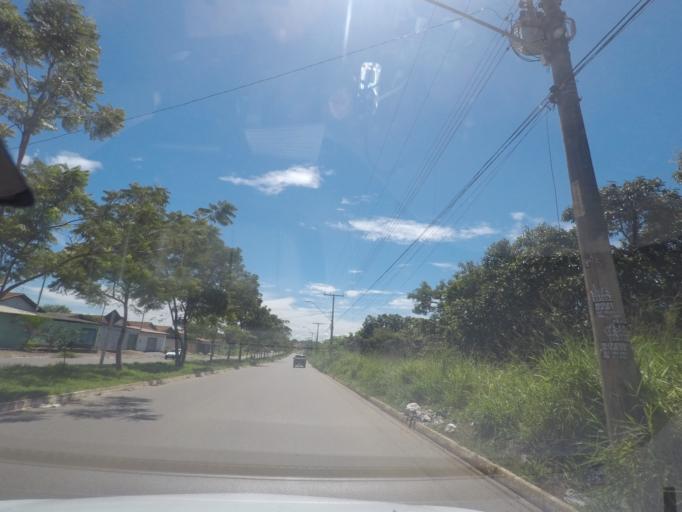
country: BR
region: Goias
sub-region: Aparecida De Goiania
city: Aparecida de Goiania
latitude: -16.7757
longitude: -49.3290
